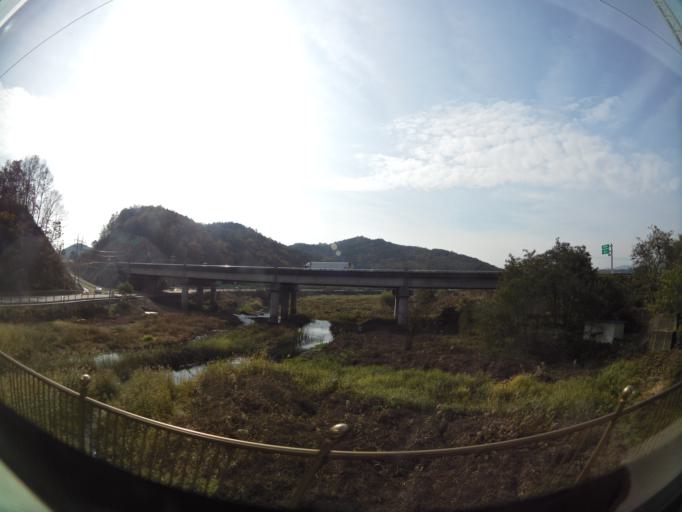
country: KR
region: Chungcheongbuk-do
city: Cheongju-si
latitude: 36.6359
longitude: 127.2869
